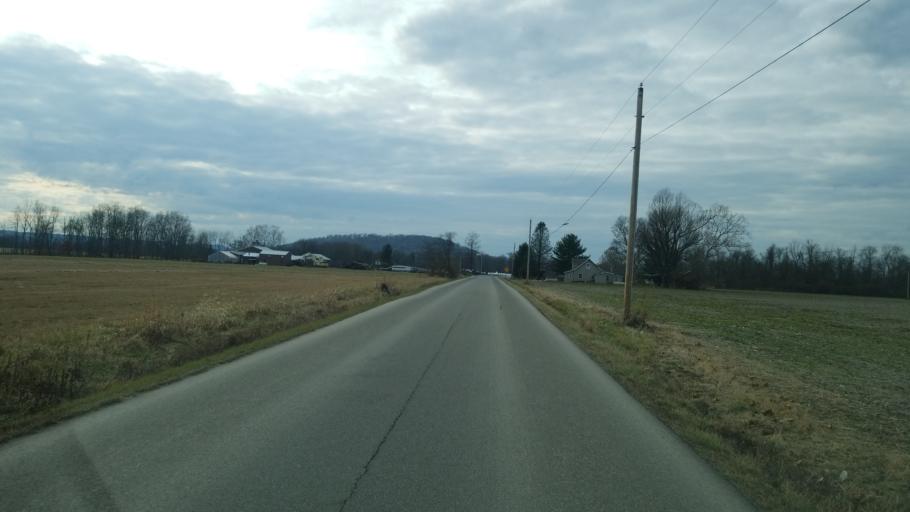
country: US
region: Ohio
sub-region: Highland County
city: Greenfield
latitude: 39.1788
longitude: -83.3079
